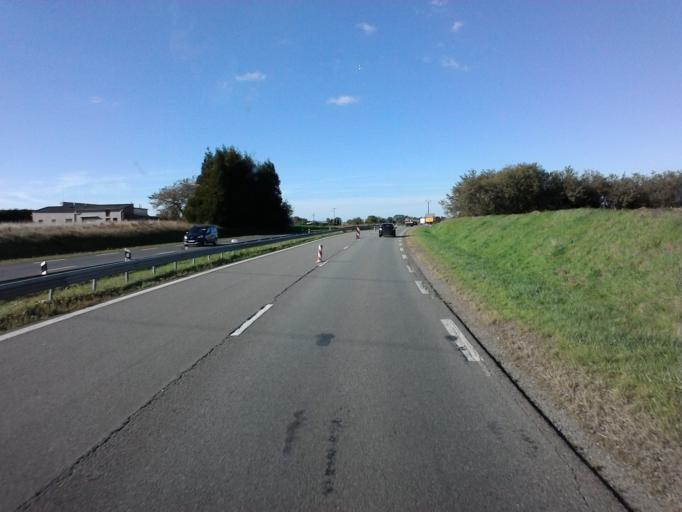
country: FR
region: Lorraine
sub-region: Departement de Meurthe-et-Moselle
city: Haucourt-Moulaine
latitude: 49.4844
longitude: 5.8152
